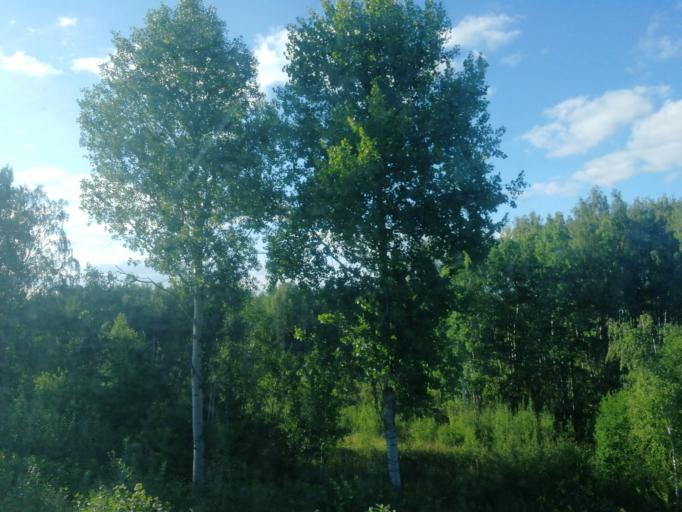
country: RU
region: Tula
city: Novogurovskiy
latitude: 54.2800
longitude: 37.2102
